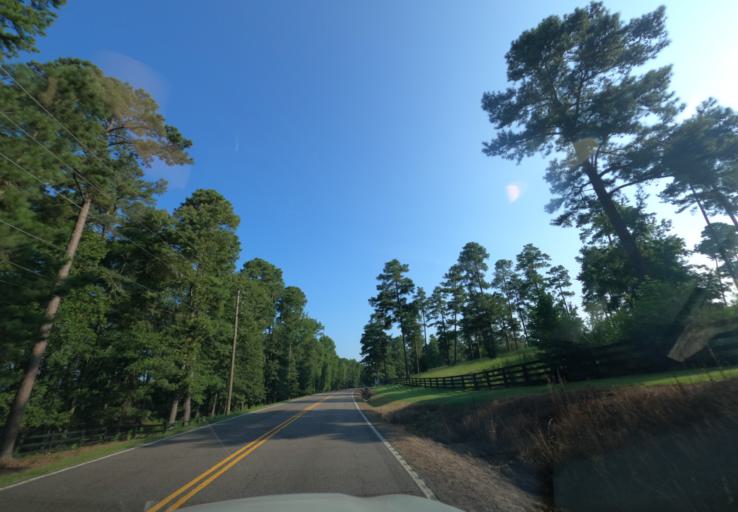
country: US
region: South Carolina
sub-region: Edgefield County
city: Murphys Estates
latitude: 33.6699
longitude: -81.9782
